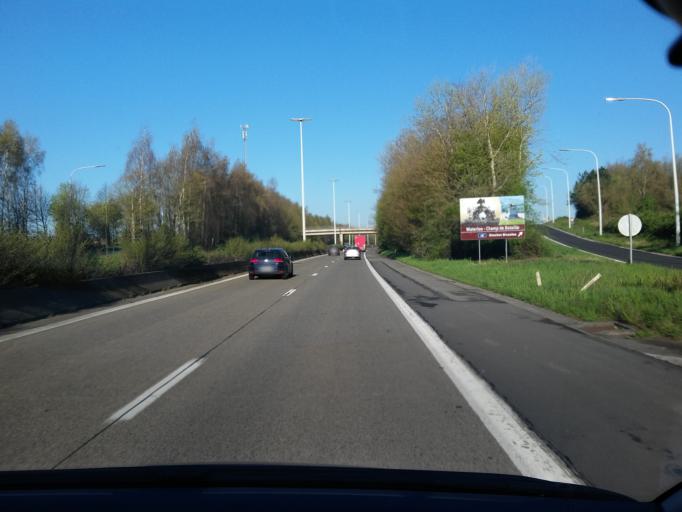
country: BE
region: Wallonia
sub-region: Province du Brabant Wallon
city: Genappe
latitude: 50.6186
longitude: 4.4707
